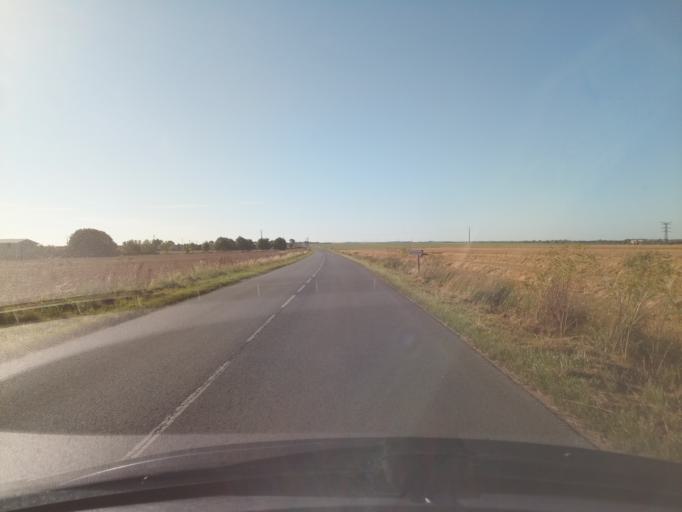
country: FR
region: Poitou-Charentes
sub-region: Departement de la Charente-Maritime
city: Marans
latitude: 46.2998
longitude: -0.9799
